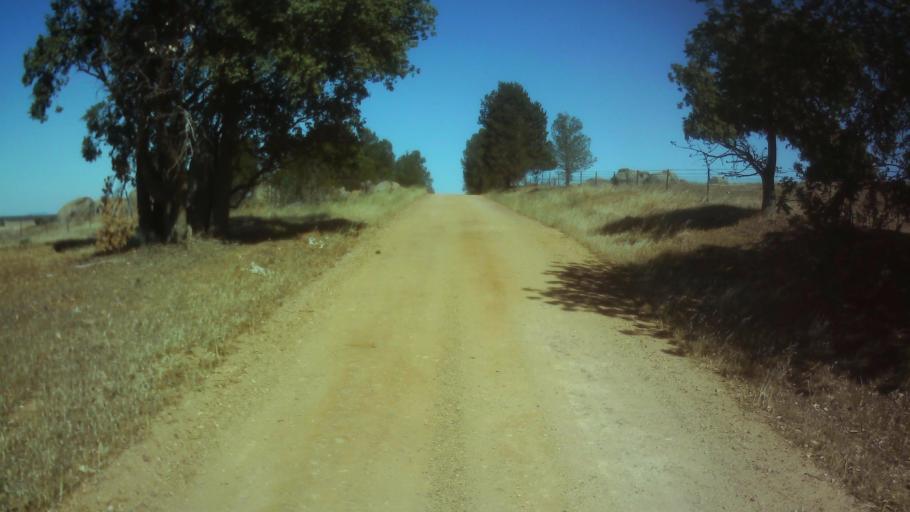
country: AU
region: New South Wales
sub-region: Weddin
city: Grenfell
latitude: -33.9927
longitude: 148.3466
